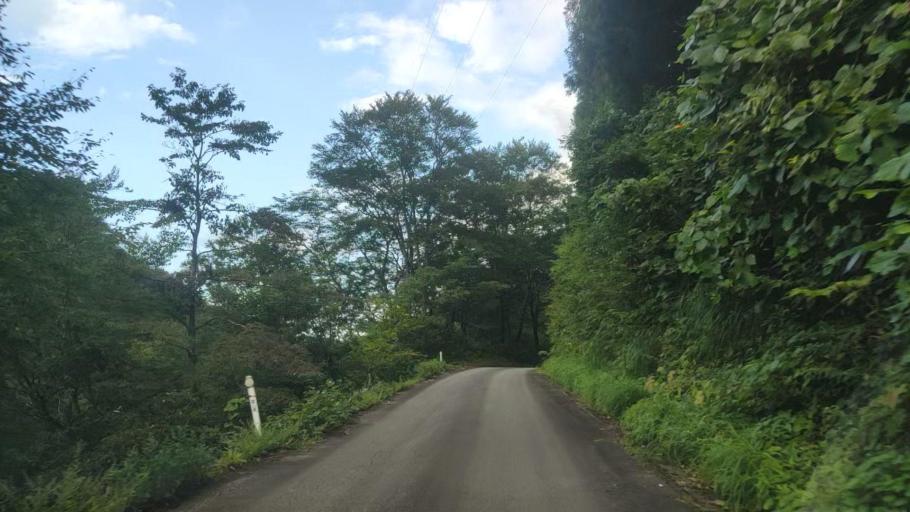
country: JP
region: Toyama
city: Yatsuomachi-higashikumisaka
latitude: 36.4197
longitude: 137.0819
